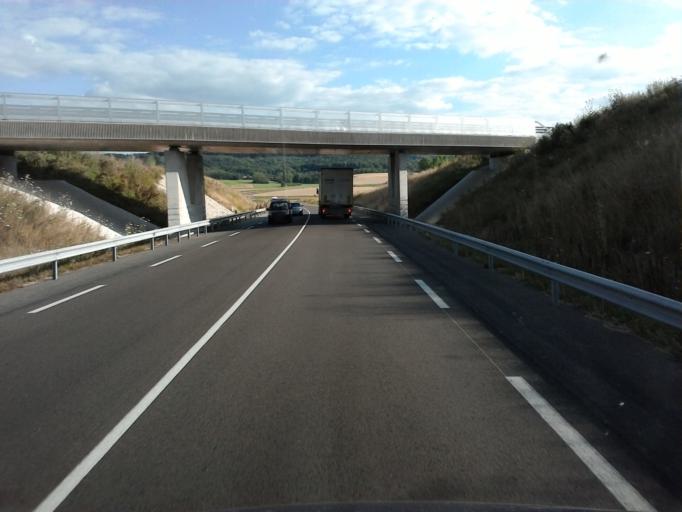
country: FR
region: Franche-Comte
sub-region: Departement de la Haute-Saone
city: Frotey-les-Vesoul
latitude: 47.6920
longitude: 6.2666
